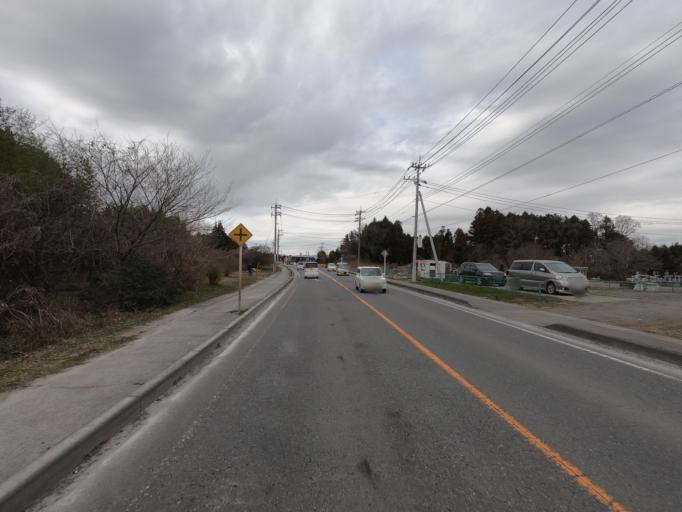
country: JP
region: Ibaraki
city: Ishioka
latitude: 36.0944
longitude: 140.3013
